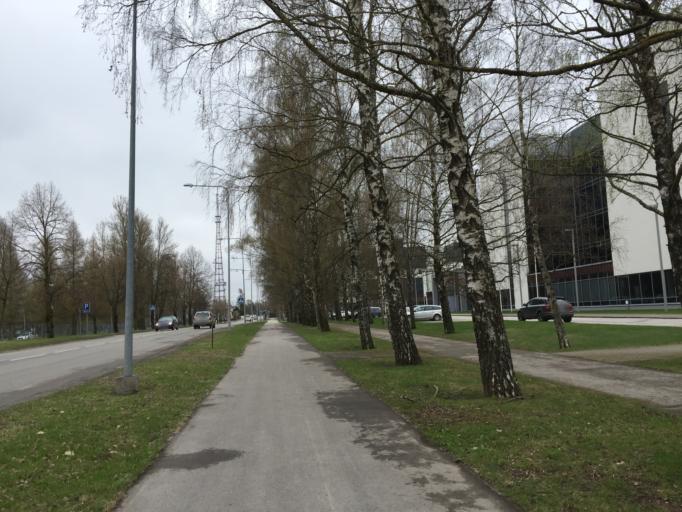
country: EE
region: Tartu
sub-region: Tartu linn
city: Tartu
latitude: 58.3680
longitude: 26.6930
